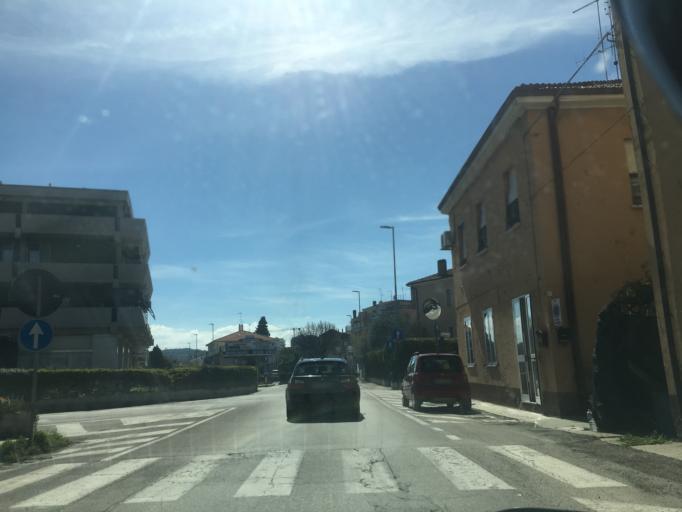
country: IT
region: The Marches
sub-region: Provincia di Pesaro e Urbino
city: Pesaro
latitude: 43.9101
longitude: 12.8957
